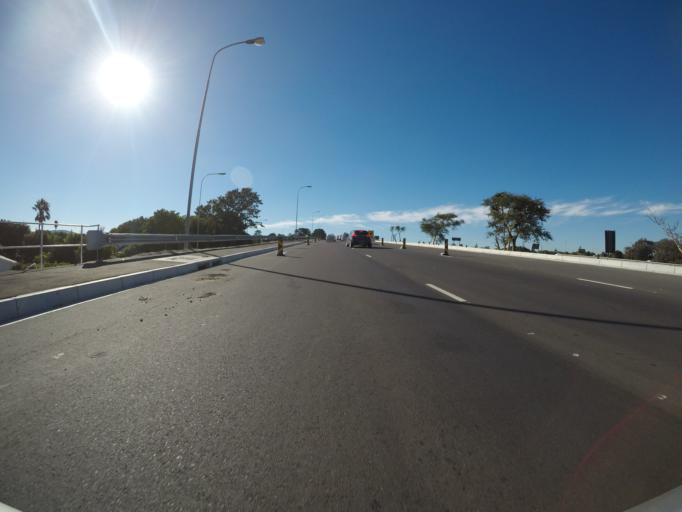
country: ZA
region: Western Cape
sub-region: City of Cape Town
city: Kraaifontein
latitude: -33.8783
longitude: 18.6600
